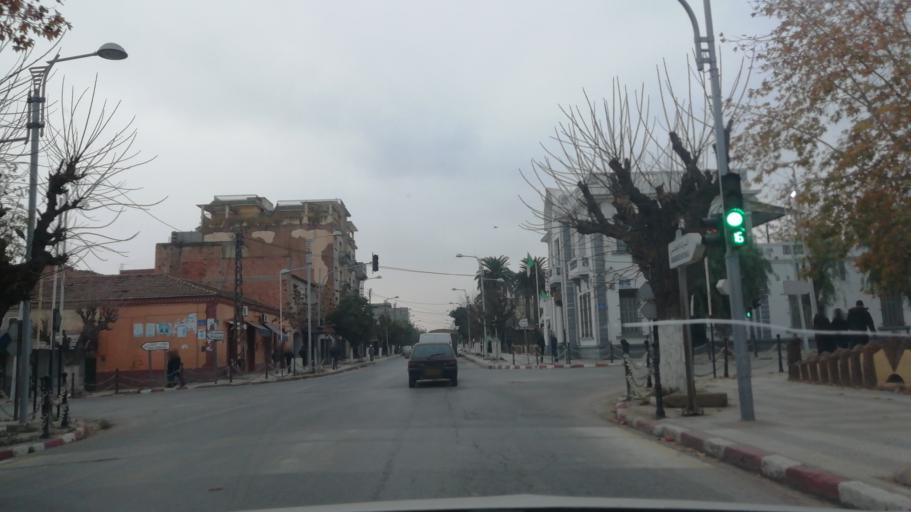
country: DZ
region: Sidi Bel Abbes
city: Sfizef
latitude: 35.2354
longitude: -0.2425
